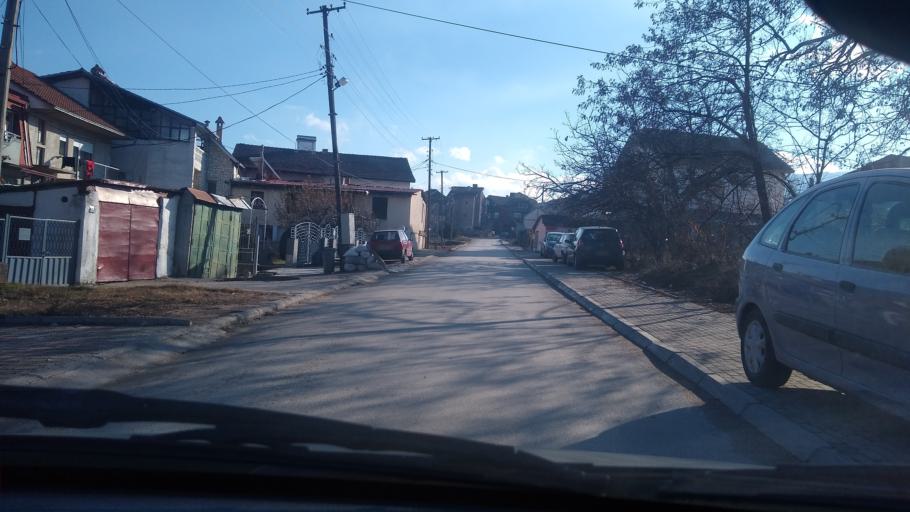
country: MK
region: Bitola
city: Bitola
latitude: 41.0092
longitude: 21.3455
